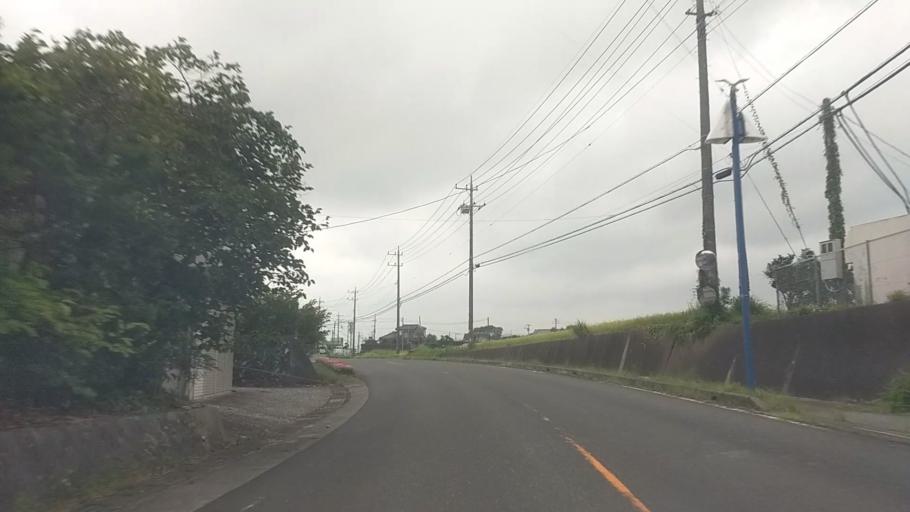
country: JP
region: Chiba
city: Kawaguchi
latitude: 35.1153
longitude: 140.0795
